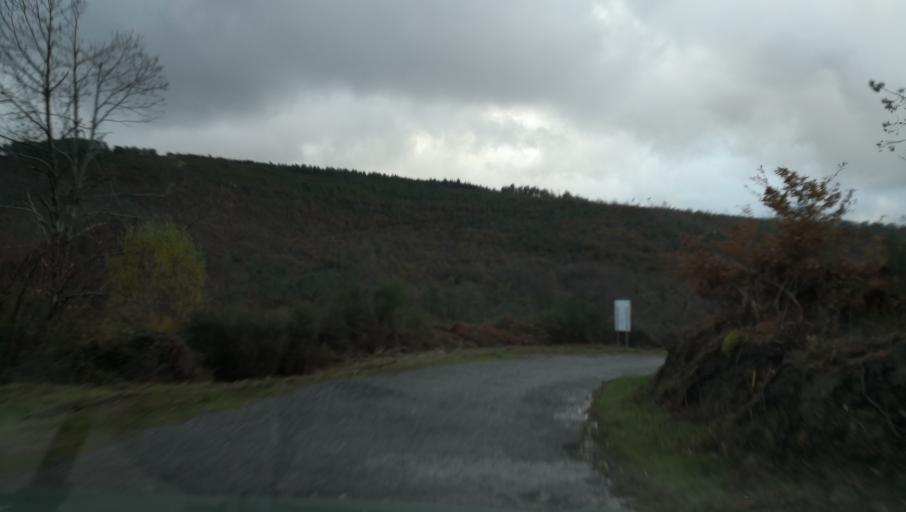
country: PT
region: Vila Real
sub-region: Santa Marta de Penaguiao
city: Santa Marta de Penaguiao
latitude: 41.3062
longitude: -7.8672
